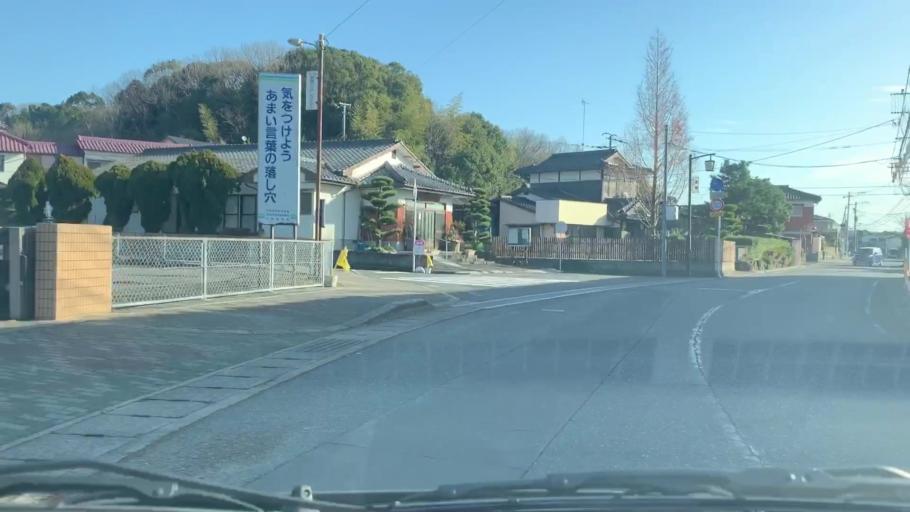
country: JP
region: Saga Prefecture
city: Takeocho-takeo
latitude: 33.2209
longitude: 130.0623
